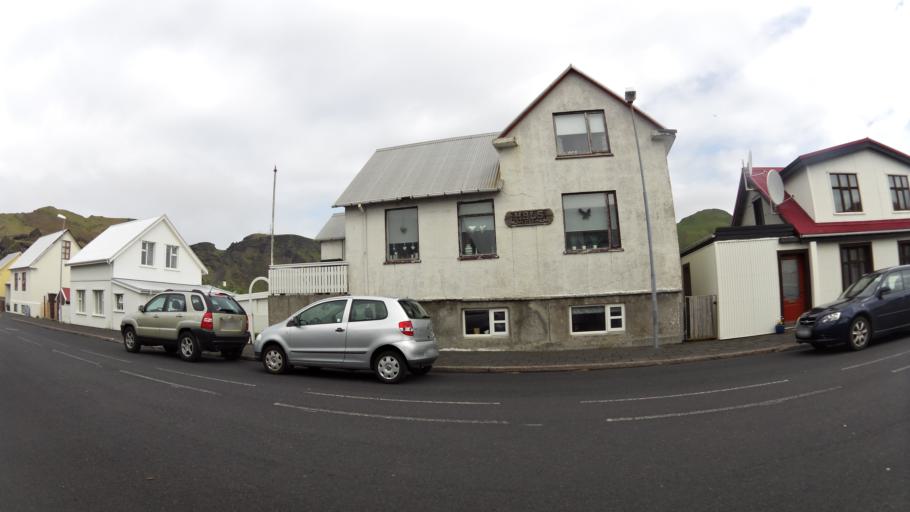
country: IS
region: South
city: Vestmannaeyjar
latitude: 63.4387
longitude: -20.2746
